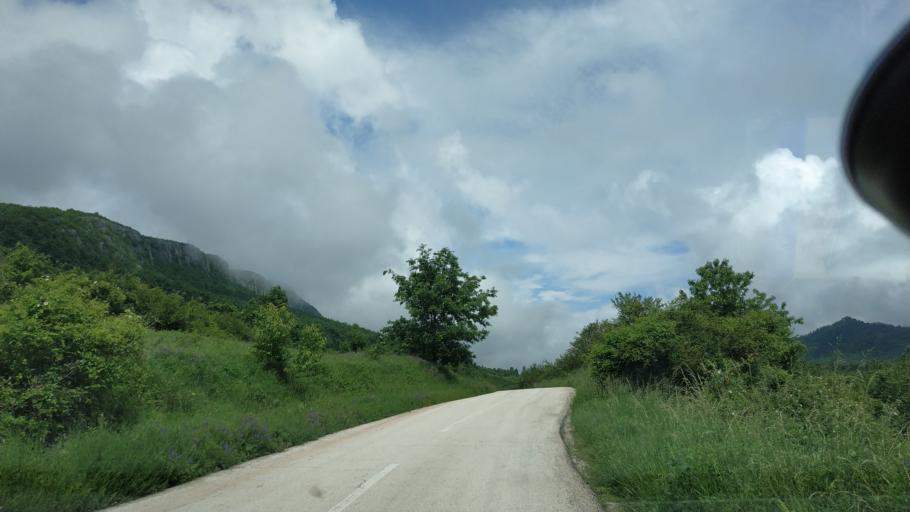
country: RS
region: Central Serbia
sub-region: Zajecarski Okrug
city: Boljevac
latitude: 43.7490
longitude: 21.9460
